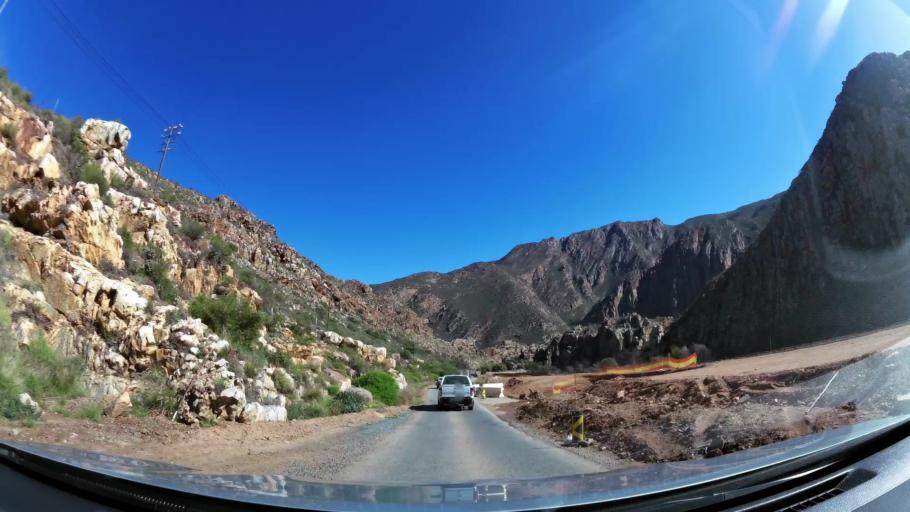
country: ZA
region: Western Cape
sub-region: Cape Winelands District Municipality
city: Ashton
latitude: -33.8030
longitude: 20.0991
